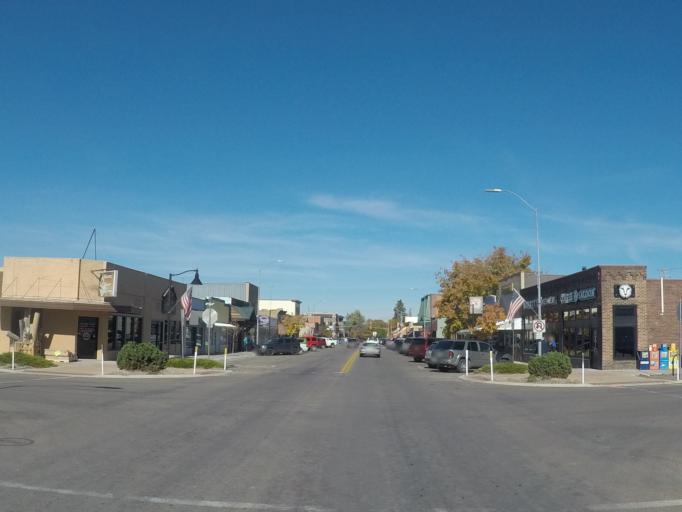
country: US
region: Montana
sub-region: Lake County
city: Polson
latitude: 47.6922
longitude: -114.1634
